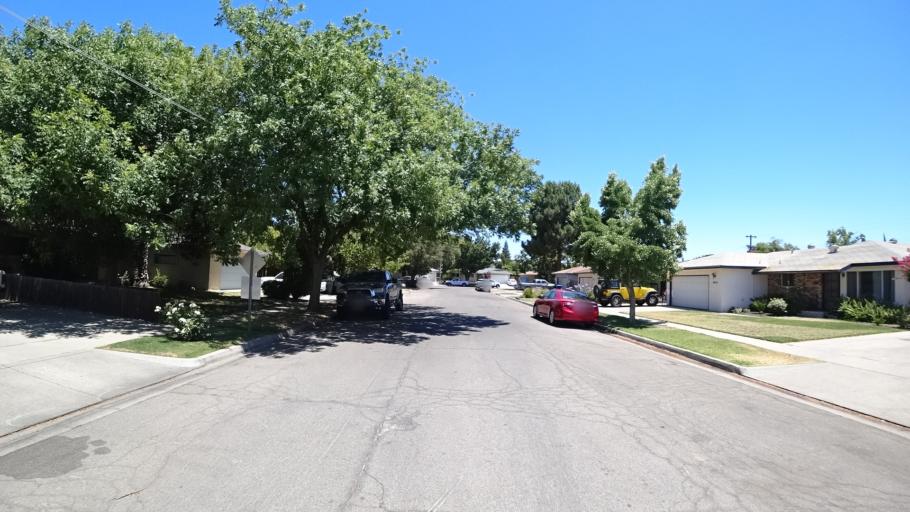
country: US
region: California
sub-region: Fresno County
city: Tarpey Village
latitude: 36.8005
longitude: -119.7505
